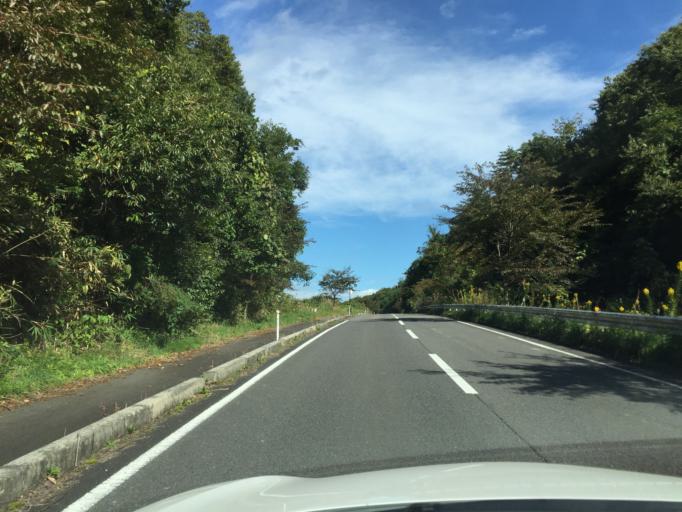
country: JP
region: Fukushima
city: Miharu
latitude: 37.4316
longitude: 140.5239
